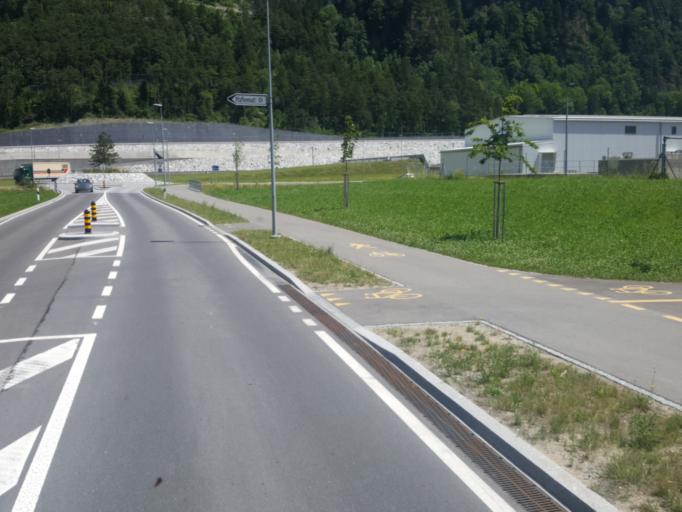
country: CH
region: Uri
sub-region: Uri
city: Erstfeld
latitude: 46.8350
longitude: 8.6407
